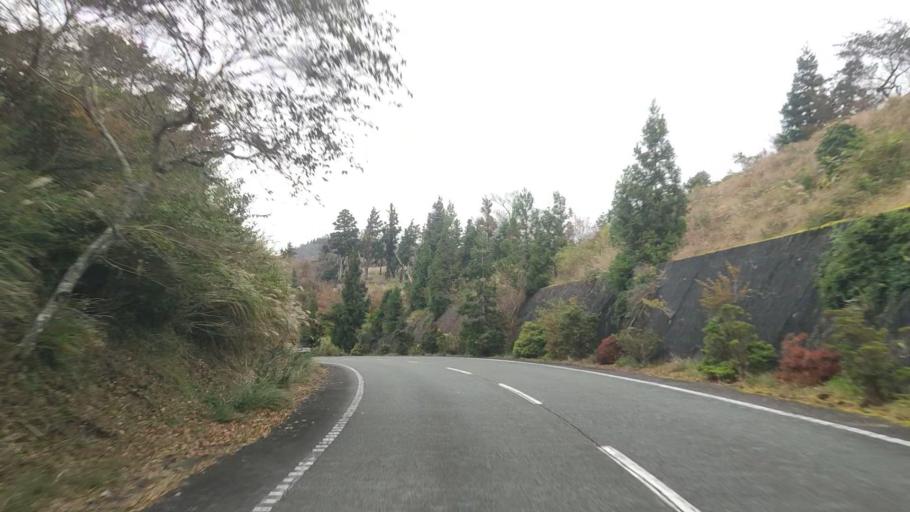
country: JP
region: Shizuoka
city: Heda
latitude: 34.9025
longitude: 138.8455
